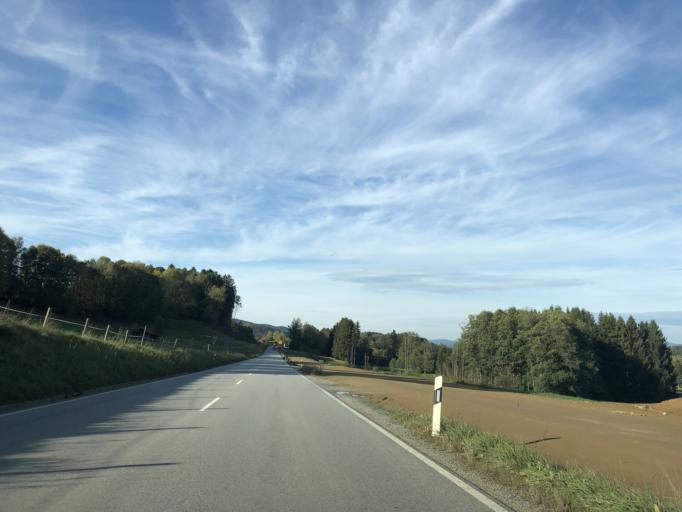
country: DE
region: Bavaria
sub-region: Lower Bavaria
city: Gotteszell
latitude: 48.9519
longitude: 12.9775
